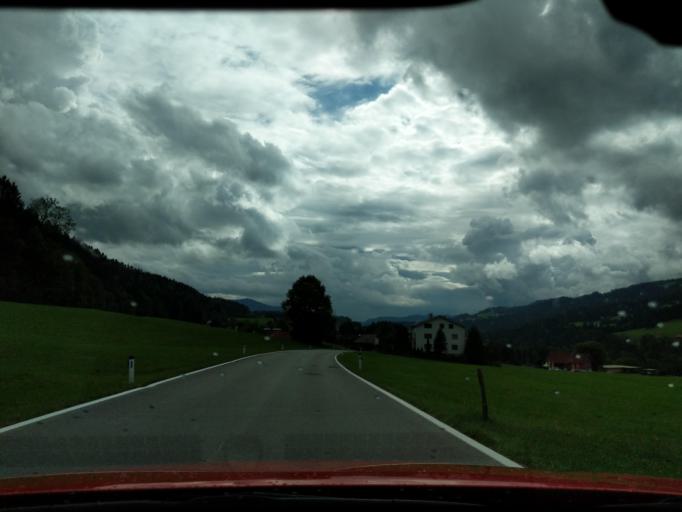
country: AT
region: Vorarlberg
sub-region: Politischer Bezirk Bregenz
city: Riefensberg
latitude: 47.5183
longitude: 9.9652
